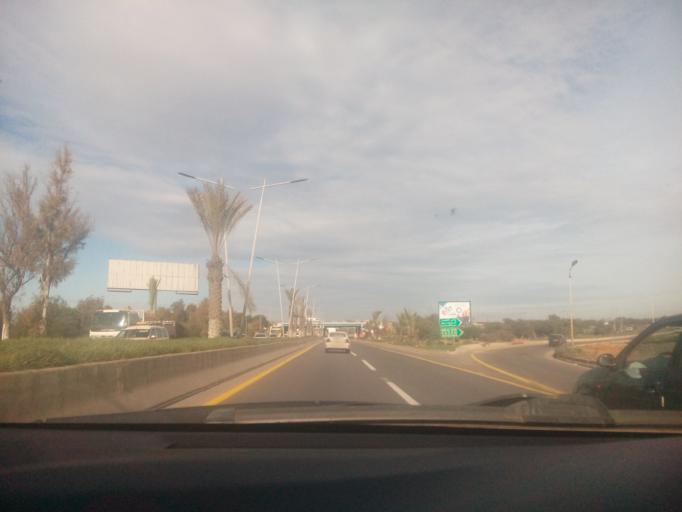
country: DZ
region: Oran
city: Es Senia
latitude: 35.6650
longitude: -0.5940
